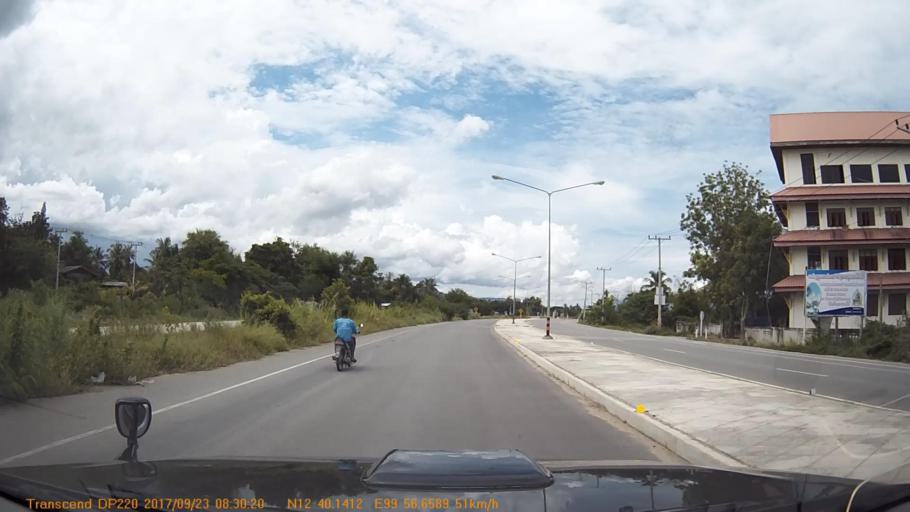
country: TH
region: Prachuap Khiri Khan
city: Hua Hin
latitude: 12.6693
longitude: 99.9442
